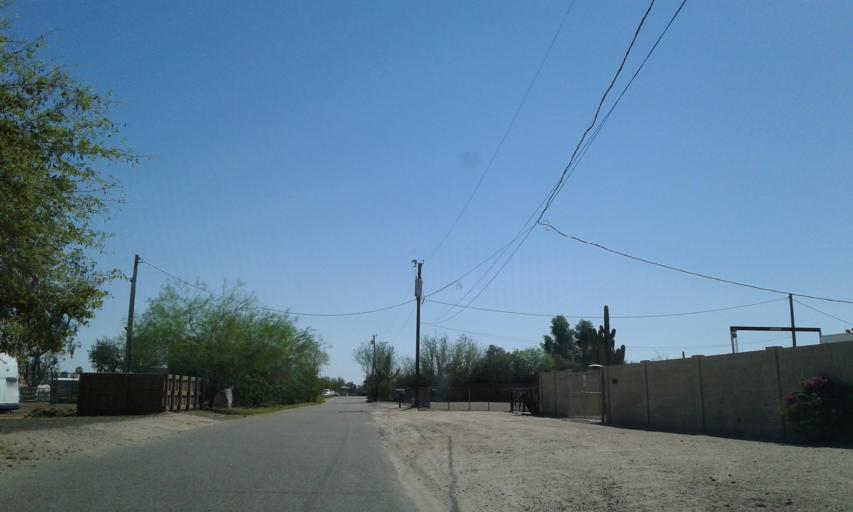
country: US
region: Arizona
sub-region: Maricopa County
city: Cave Creek
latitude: 33.6803
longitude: -112.0355
